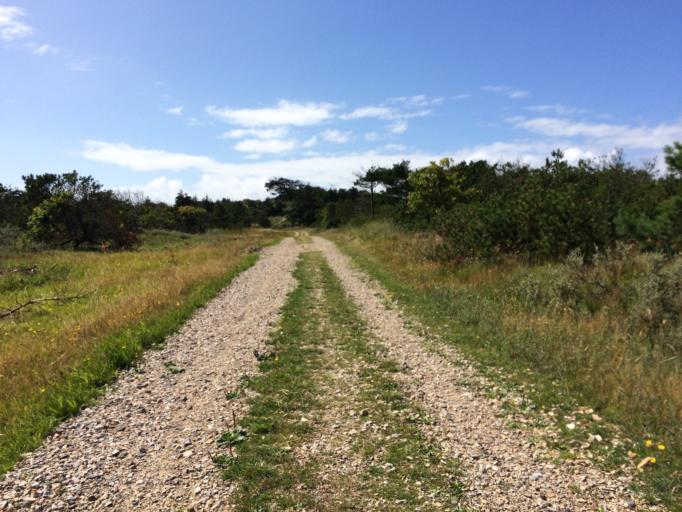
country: DK
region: Central Jutland
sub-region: Holstebro Kommune
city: Ulfborg
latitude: 56.3047
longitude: 8.1345
